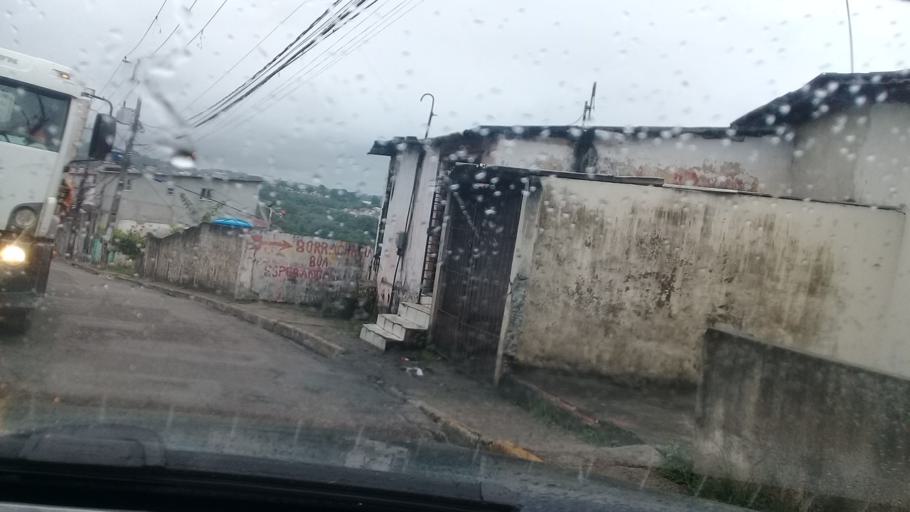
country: BR
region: Pernambuco
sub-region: Jaboatao Dos Guararapes
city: Jaboatao dos Guararapes
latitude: -8.0842
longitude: -34.9769
